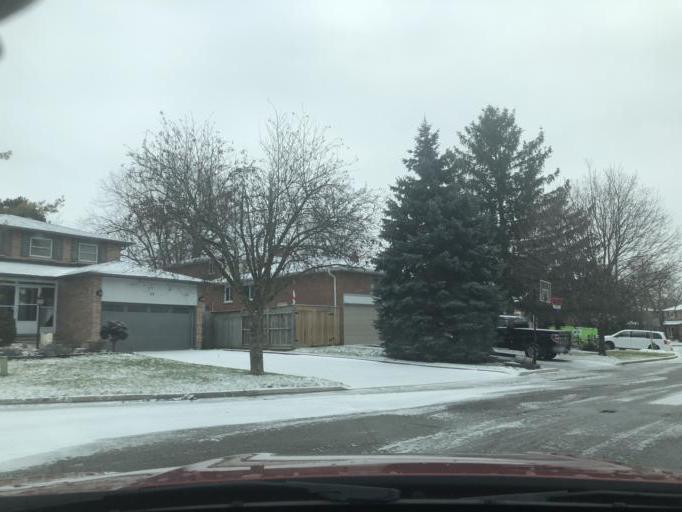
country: CA
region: Ontario
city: Markham
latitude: 43.8747
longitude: -79.2367
